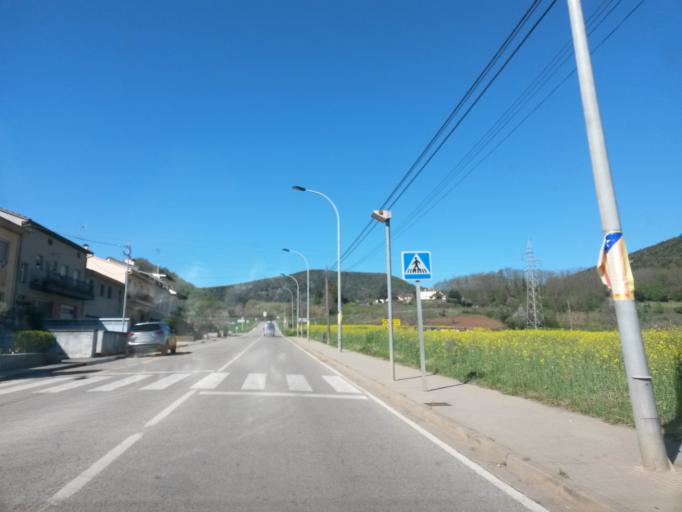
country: ES
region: Catalonia
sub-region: Provincia de Girona
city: Santa Pau
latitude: 42.1457
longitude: 2.5667
